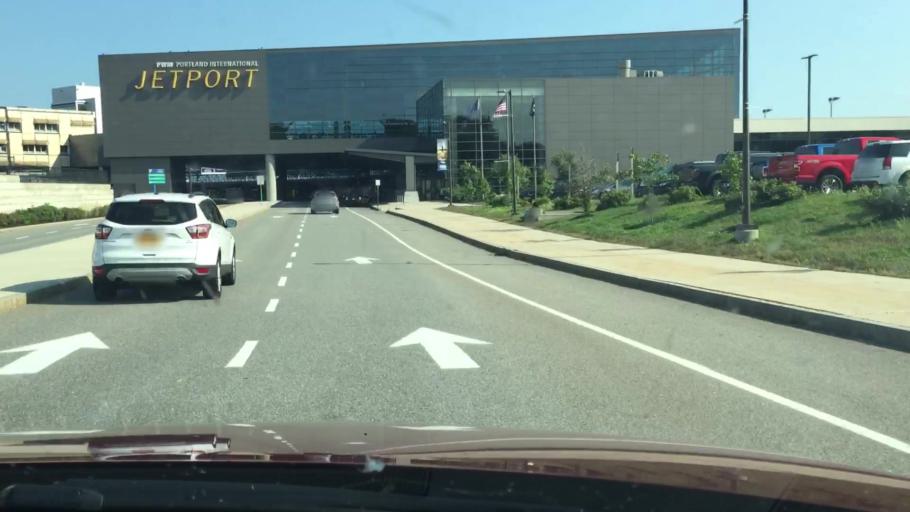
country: US
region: Maine
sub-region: Cumberland County
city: South Portland Gardens
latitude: 43.6488
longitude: -70.3127
